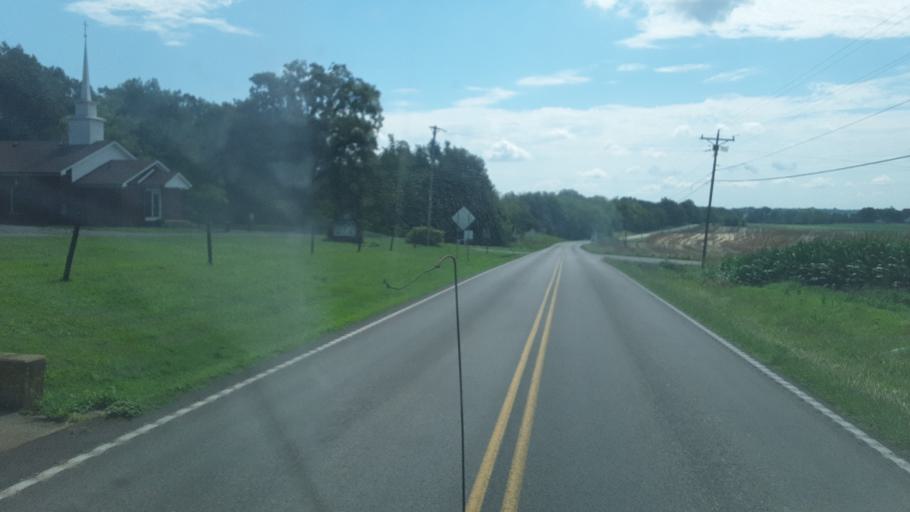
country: US
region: Kentucky
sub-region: Christian County
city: Oak Grove
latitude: 36.7540
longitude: -87.3176
